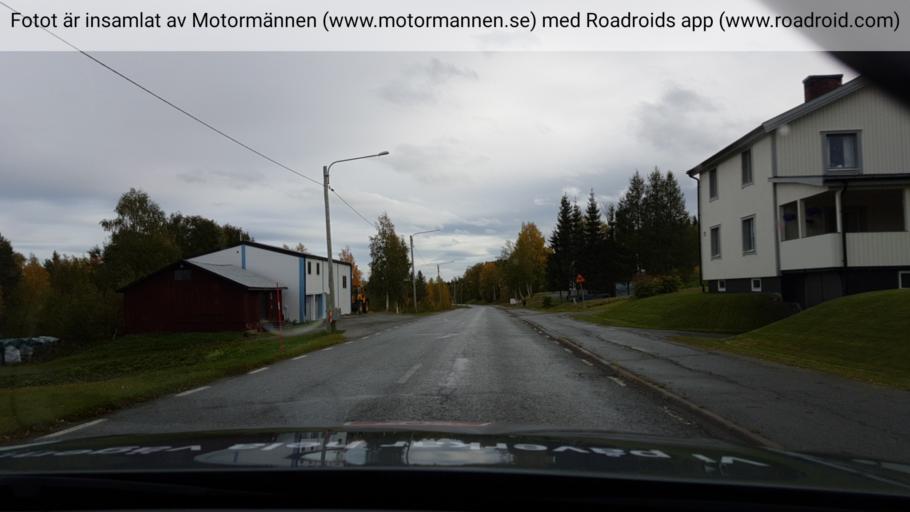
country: SE
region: Vaesterbotten
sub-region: Vilhelmina Kommun
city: Sjoberg
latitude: 64.6361
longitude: 16.3698
